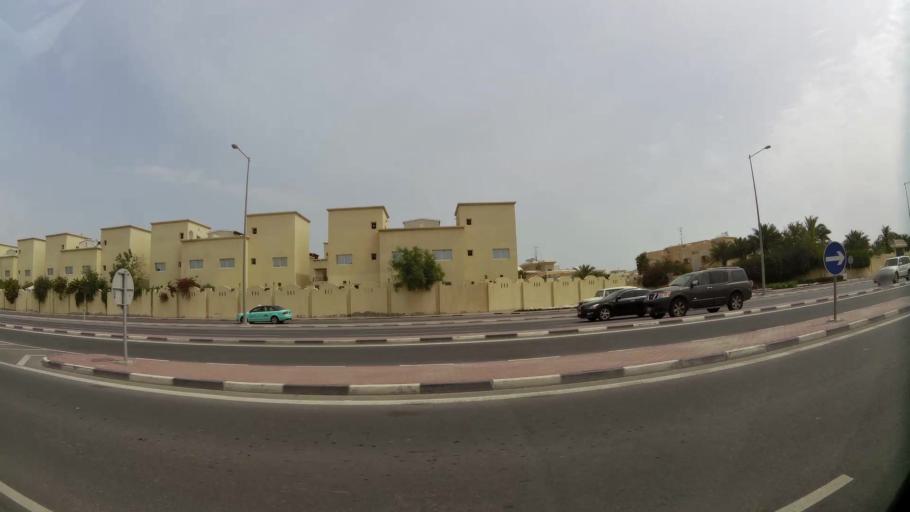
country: QA
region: Baladiyat ad Dawhah
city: Doha
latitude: 25.2458
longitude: 51.4924
